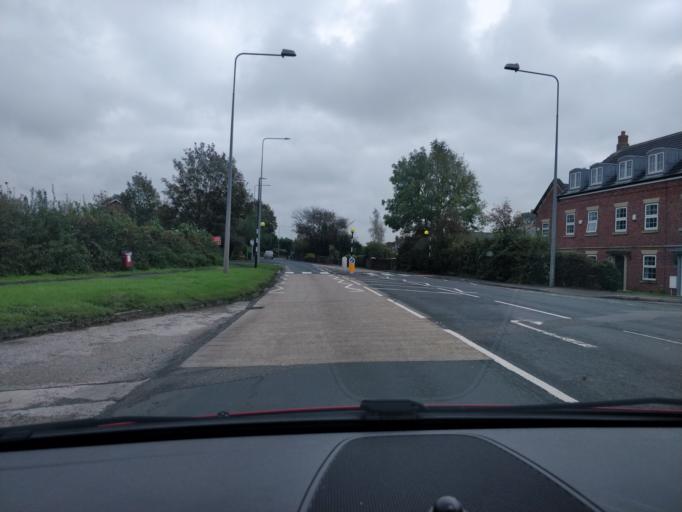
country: GB
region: England
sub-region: Sefton
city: Southport
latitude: 53.6205
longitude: -2.9547
